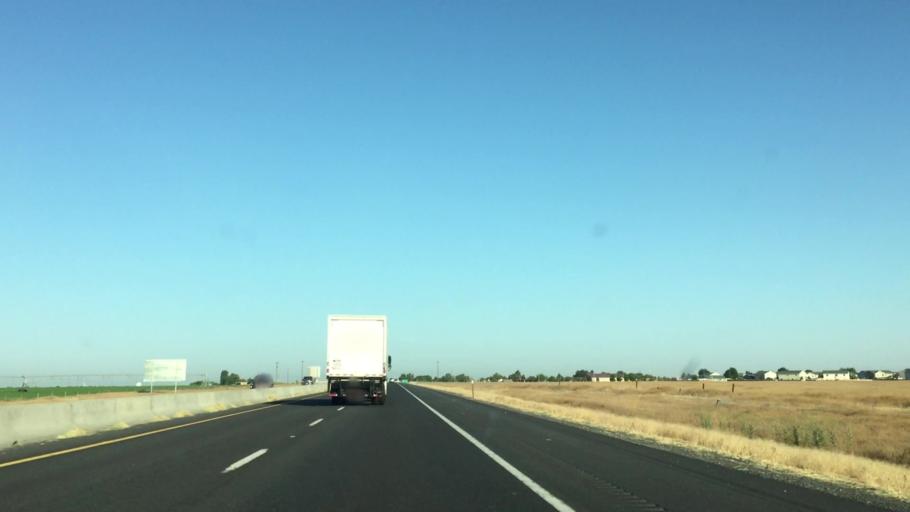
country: US
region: Washington
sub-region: Grant County
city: Moses Lake
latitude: 47.1017
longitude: -119.2643
